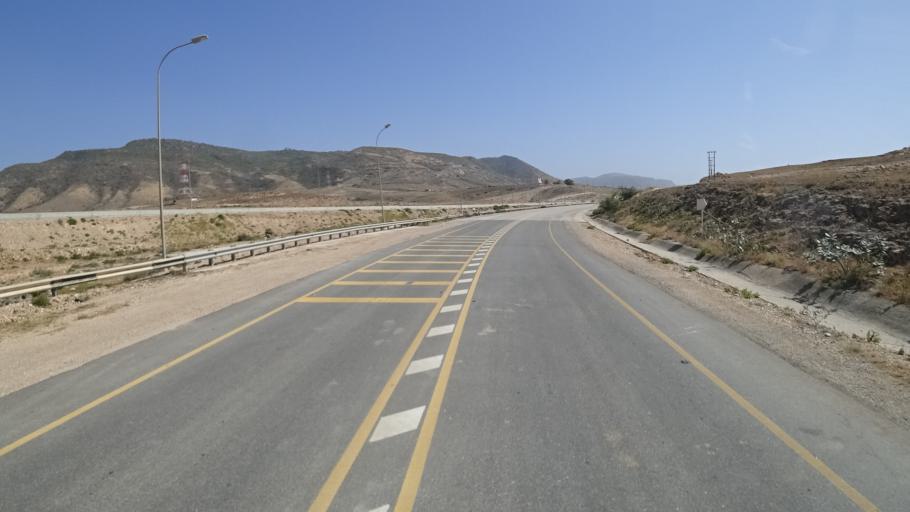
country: OM
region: Zufar
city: Salalah
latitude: 17.0588
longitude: 54.4328
